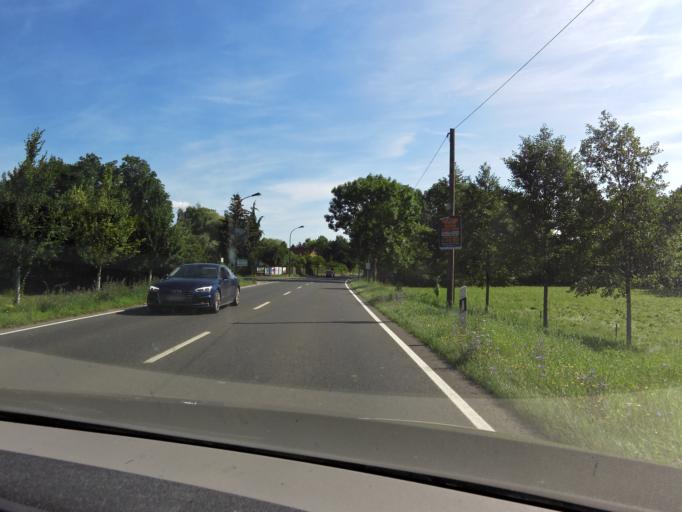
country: DE
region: Saxony
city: Markkleeberg
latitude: 51.2758
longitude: 12.3895
